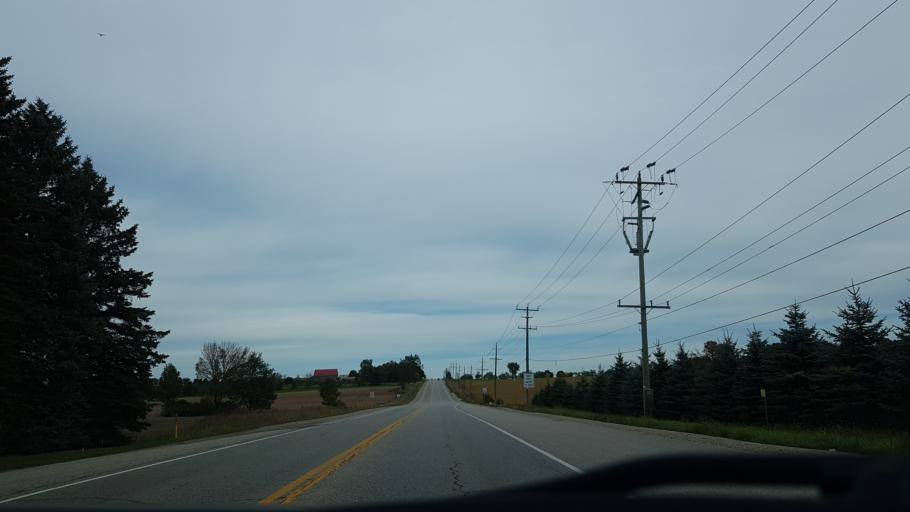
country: CA
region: Ontario
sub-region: Wellington County
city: Guelph
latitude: 43.6519
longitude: -80.1827
